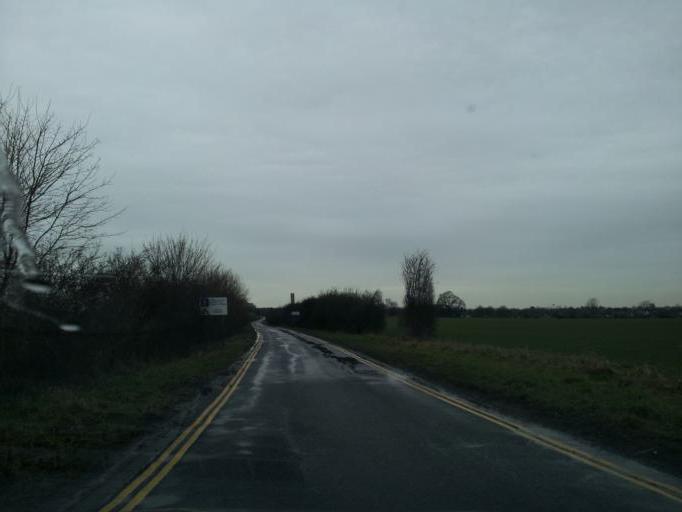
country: GB
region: England
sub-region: Cambridgeshire
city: Sawston
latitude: 52.1724
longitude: 0.1632
